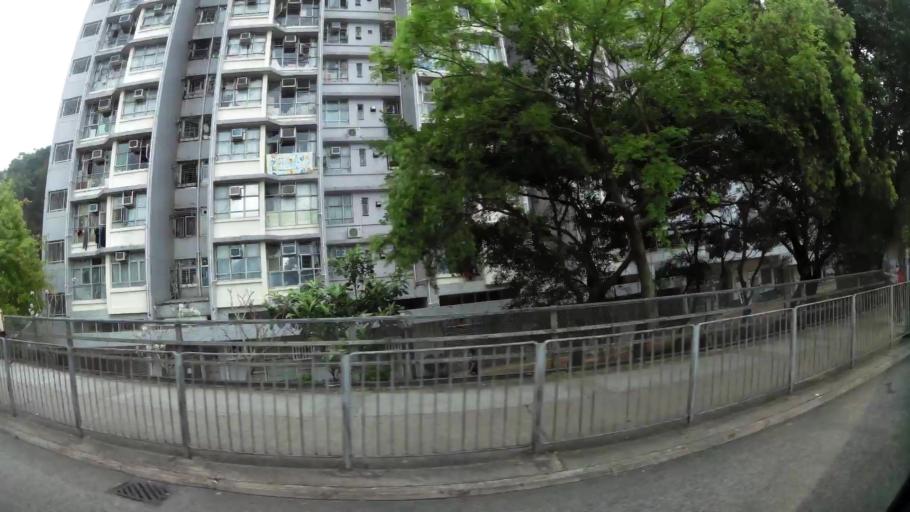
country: HK
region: Kowloon City
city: Kowloon
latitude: 22.3046
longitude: 114.2381
